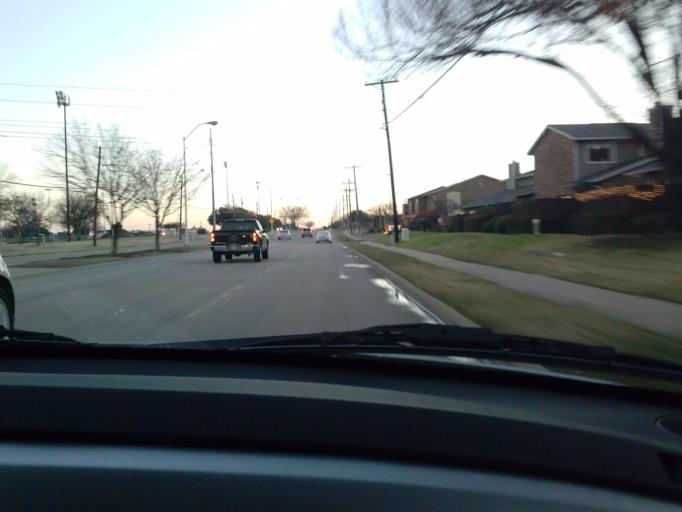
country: US
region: Texas
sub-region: Collin County
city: Plano
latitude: 33.0620
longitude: -96.7100
